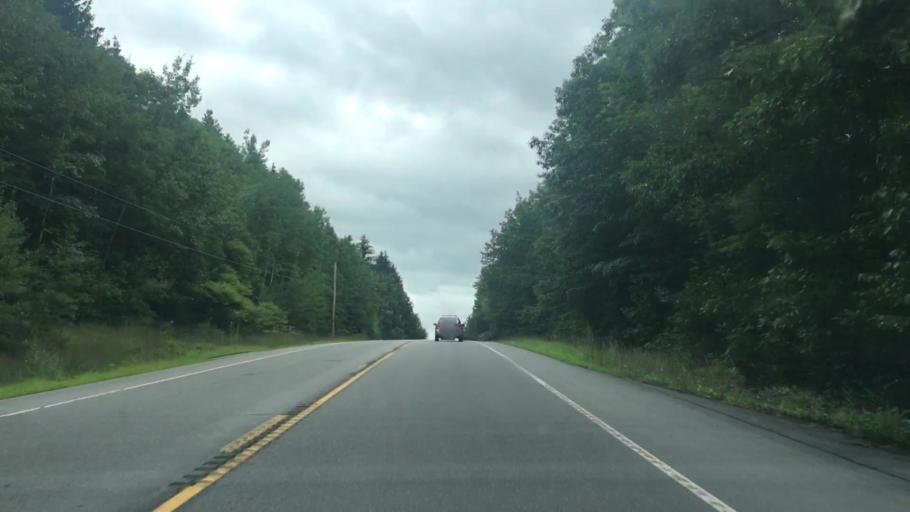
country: US
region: Maine
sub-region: York County
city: Alfred
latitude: 43.5036
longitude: -70.7175
